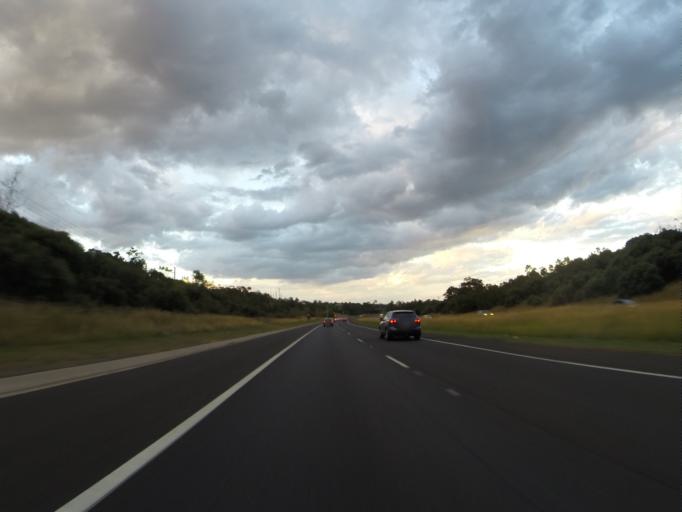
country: AU
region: New South Wales
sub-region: Campbelltown Municipality
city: Glen Alpine
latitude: -34.0673
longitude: 150.7801
